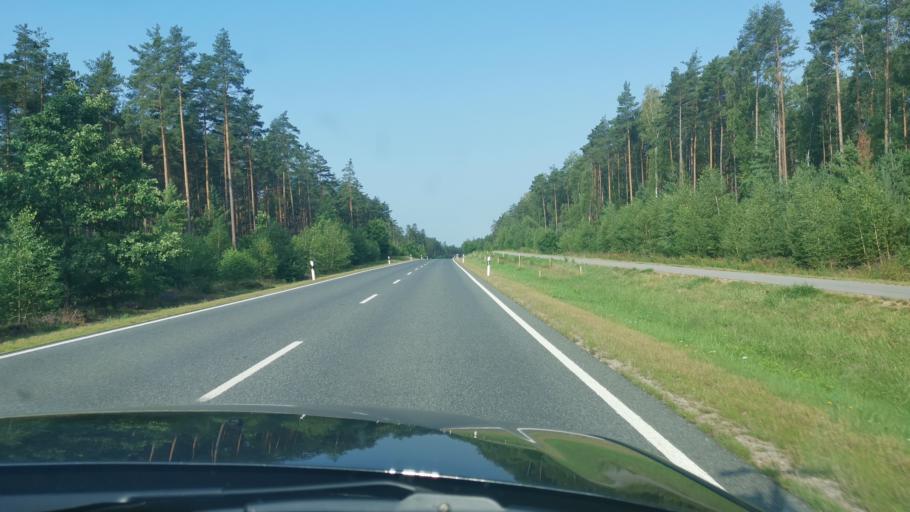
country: DE
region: Bavaria
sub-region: Upper Palatinate
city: Wernberg-Koblitz
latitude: 49.5396
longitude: 12.0932
